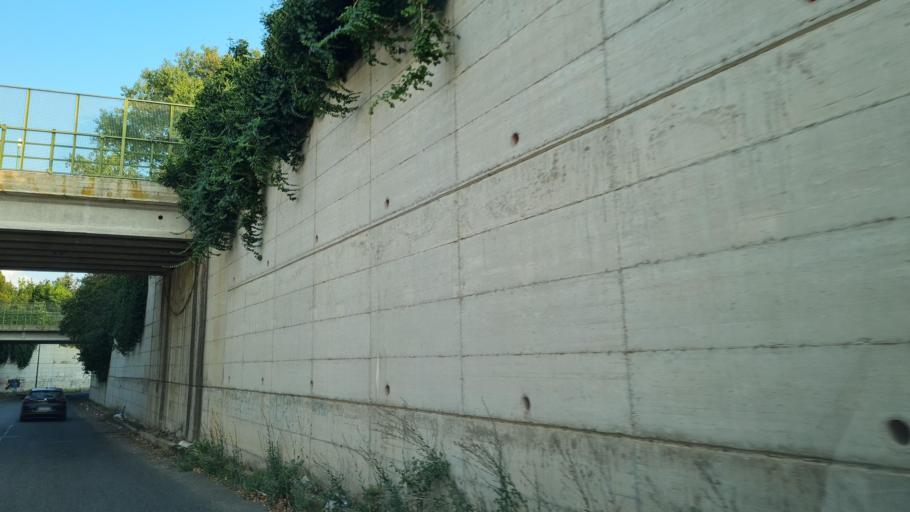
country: IT
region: Latium
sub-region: Provincia di Viterbo
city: Montalto di Castro
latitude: 42.3266
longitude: 11.6180
